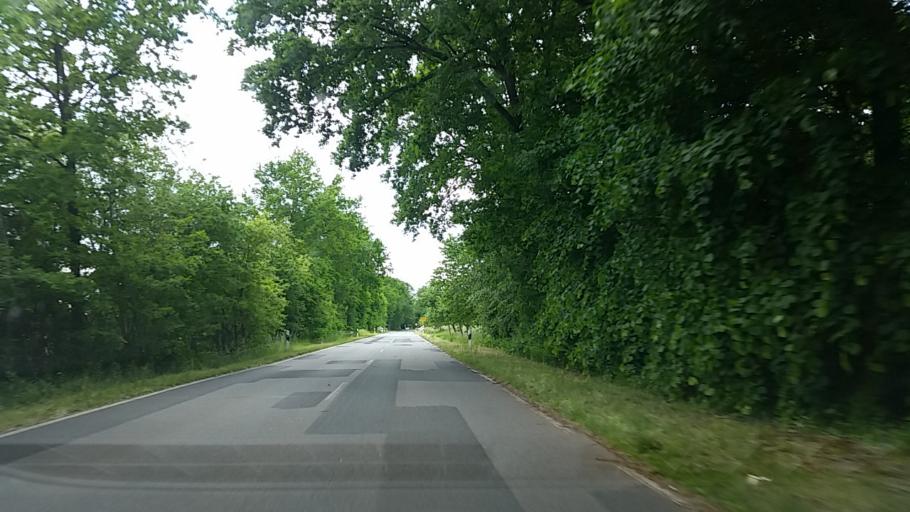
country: DE
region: Schleswig-Holstein
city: Kuddeworde
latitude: 53.5901
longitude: 10.4126
